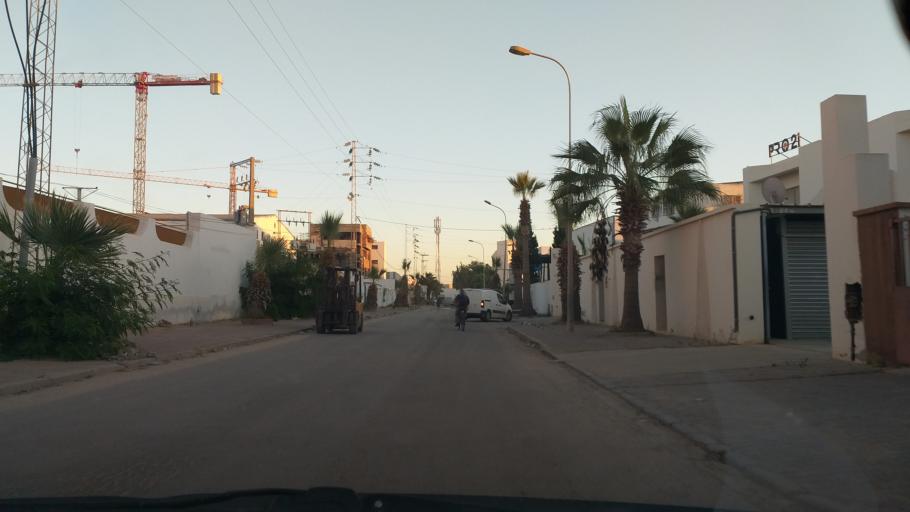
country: TN
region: Safaqis
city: Al Qarmadah
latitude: 34.7632
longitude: 10.7783
